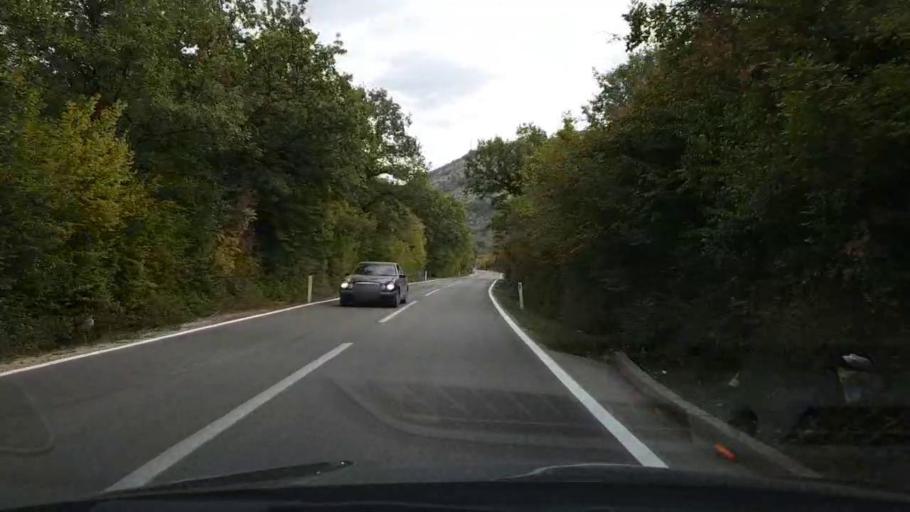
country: BA
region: Republika Srpska
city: Trebinje
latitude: 42.6861
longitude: 18.2867
